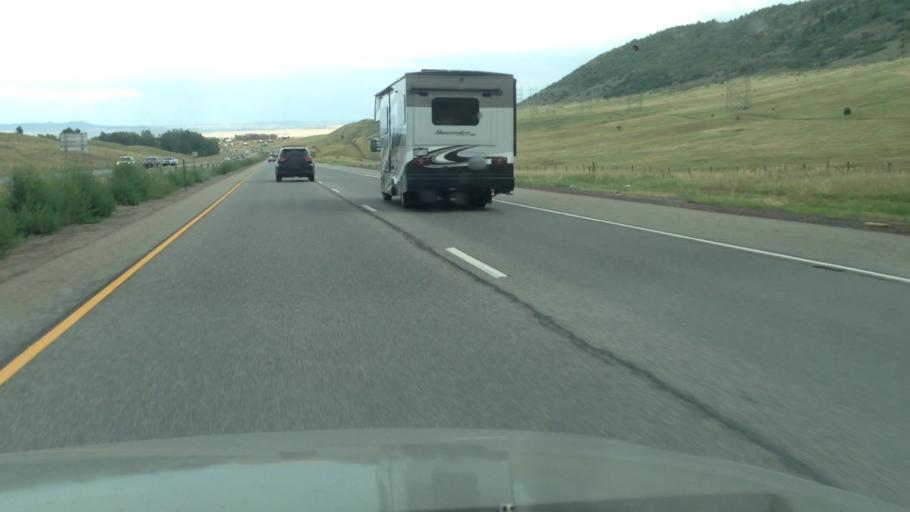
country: US
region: Colorado
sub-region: Jefferson County
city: Ken Caryl
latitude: 39.5718
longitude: -105.1367
